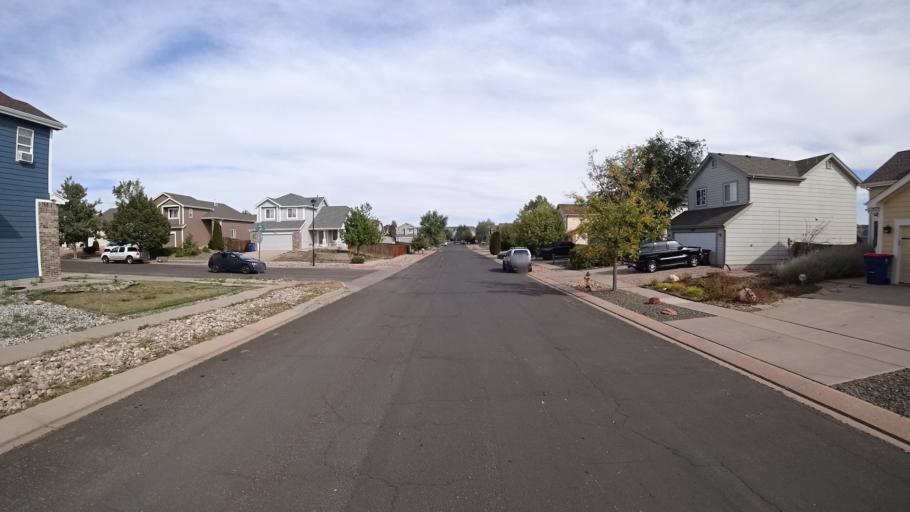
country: US
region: Colorado
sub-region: El Paso County
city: Cimarron Hills
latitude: 38.9104
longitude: -104.6924
